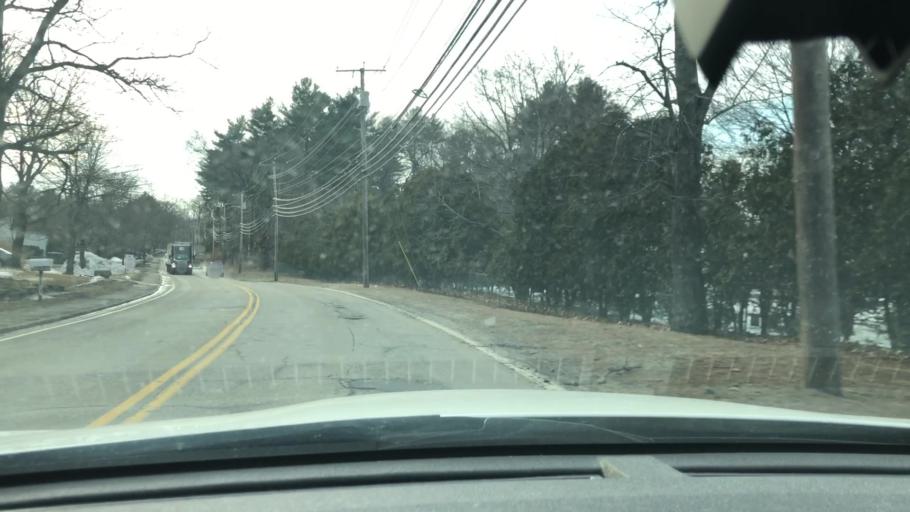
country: US
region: Massachusetts
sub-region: Middlesex County
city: Chelmsford
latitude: 42.5979
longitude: -71.3320
